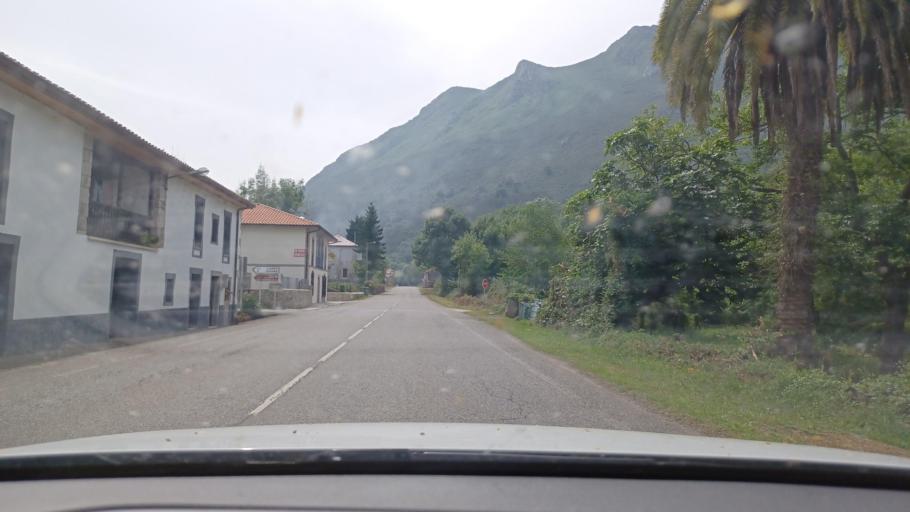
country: ES
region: Asturias
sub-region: Province of Asturias
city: Ribadesella
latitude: 43.4404
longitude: -4.9837
